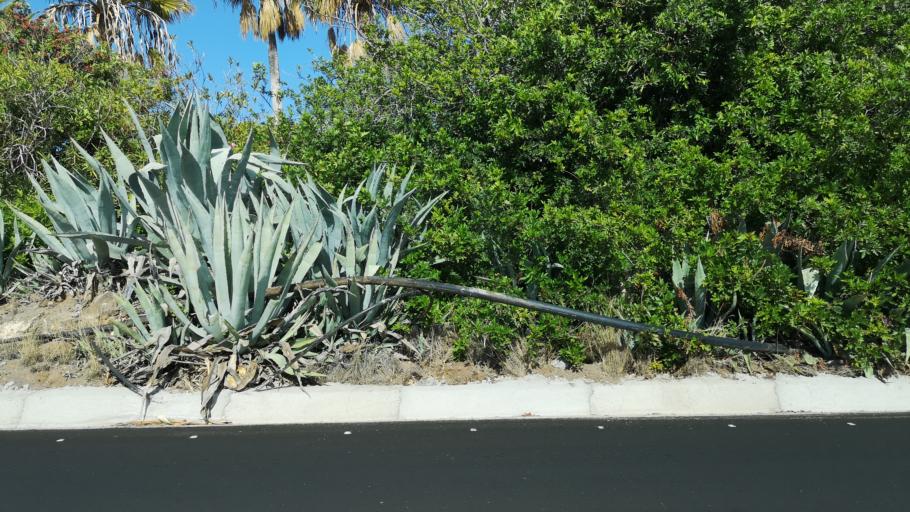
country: ES
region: Canary Islands
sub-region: Provincia de Santa Cruz de Tenerife
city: Alajero
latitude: 28.0375
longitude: -17.1946
